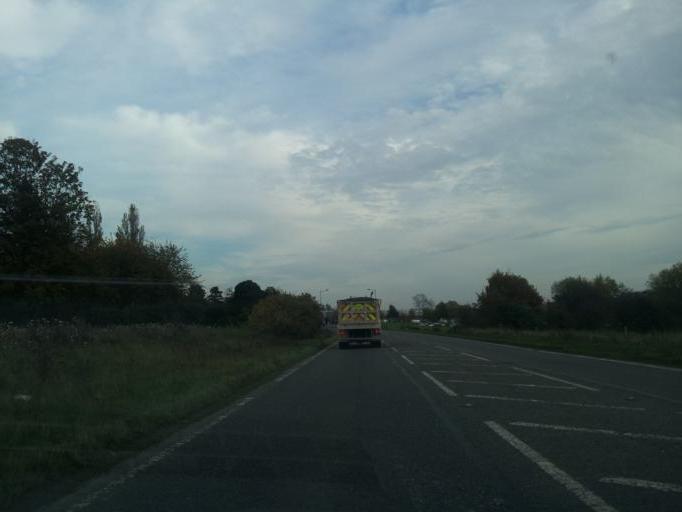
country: GB
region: England
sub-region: Cambridgeshire
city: Duxford
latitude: 52.1025
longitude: 0.1560
